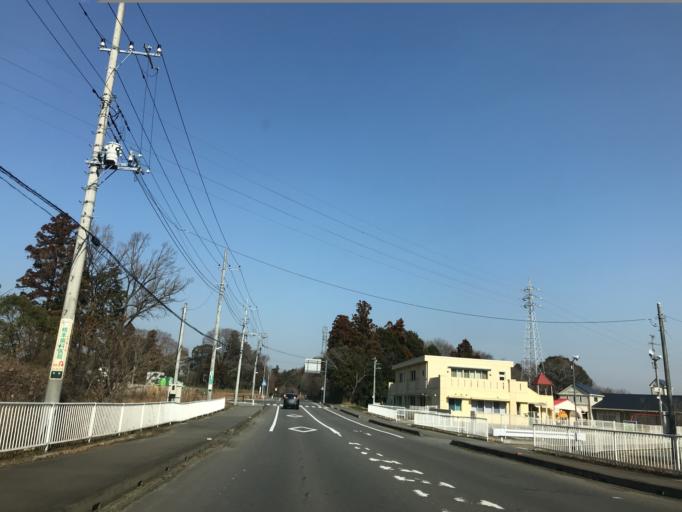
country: JP
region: Ibaraki
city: Moriya
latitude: 35.9580
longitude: 139.9975
